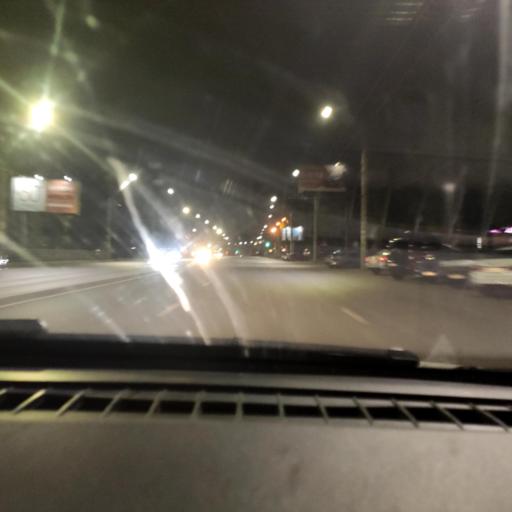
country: RU
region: Voronezj
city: Voronezh
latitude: 51.6987
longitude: 39.2728
